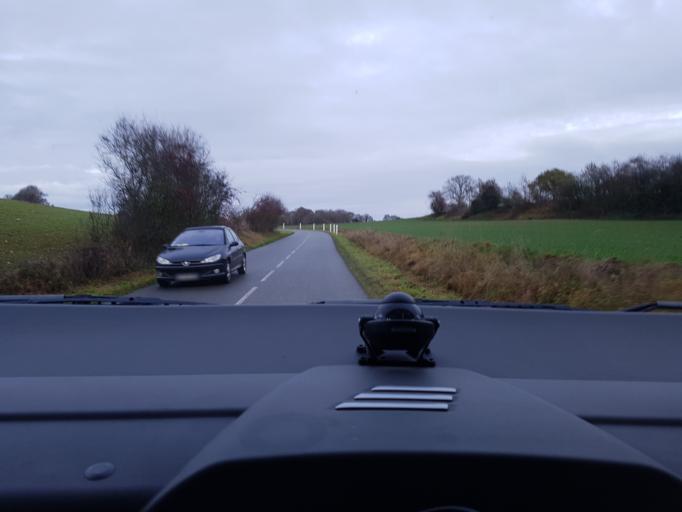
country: FR
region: Picardie
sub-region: Departement de l'Oise
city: Songeons
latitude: 49.5725
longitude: 1.8643
